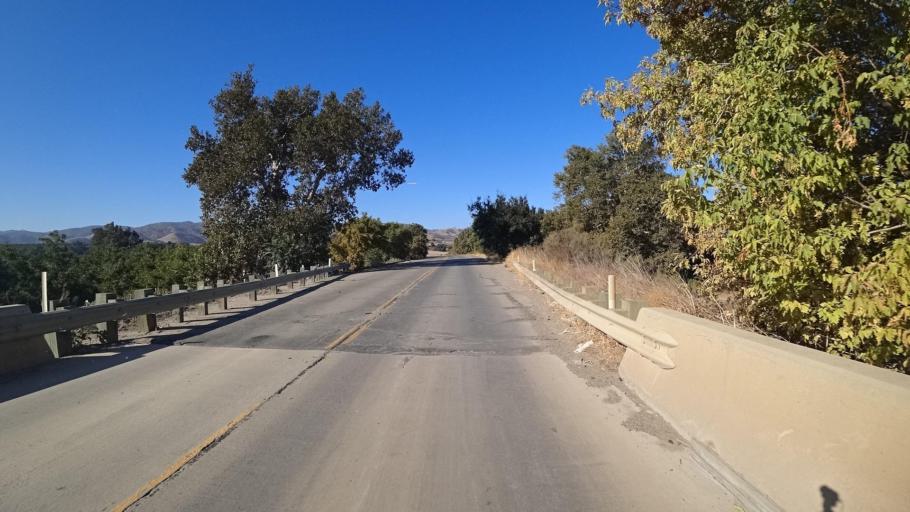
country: US
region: California
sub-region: Monterey County
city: King City
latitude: 36.0163
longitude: -120.9150
